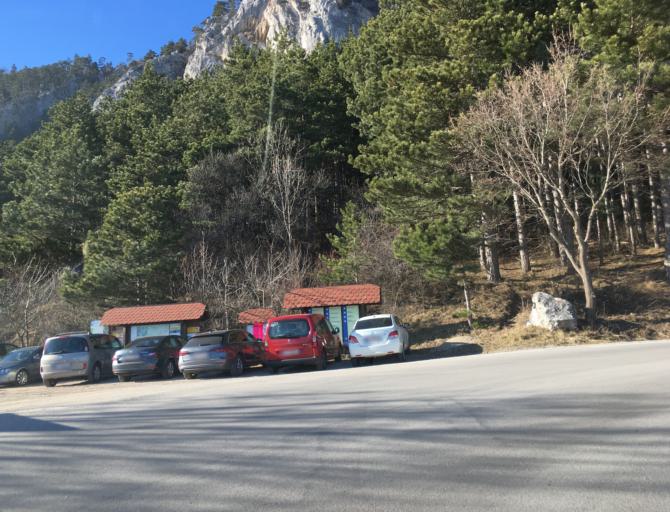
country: AT
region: Lower Austria
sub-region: Politischer Bezirk Neunkirchen
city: Willendorf am Steinfelde
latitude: 47.8280
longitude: 16.0510
